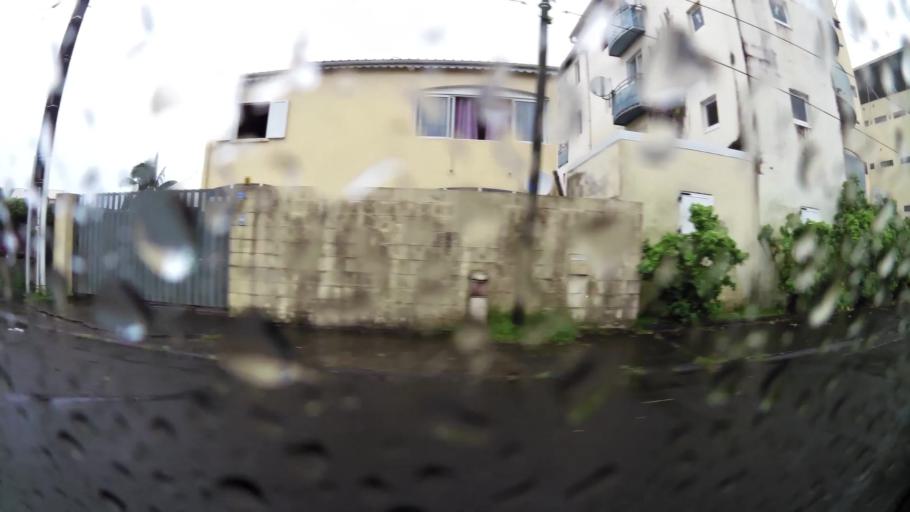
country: RE
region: Reunion
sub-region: Reunion
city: Saint-Benoit
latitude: -21.0390
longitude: 55.7138
